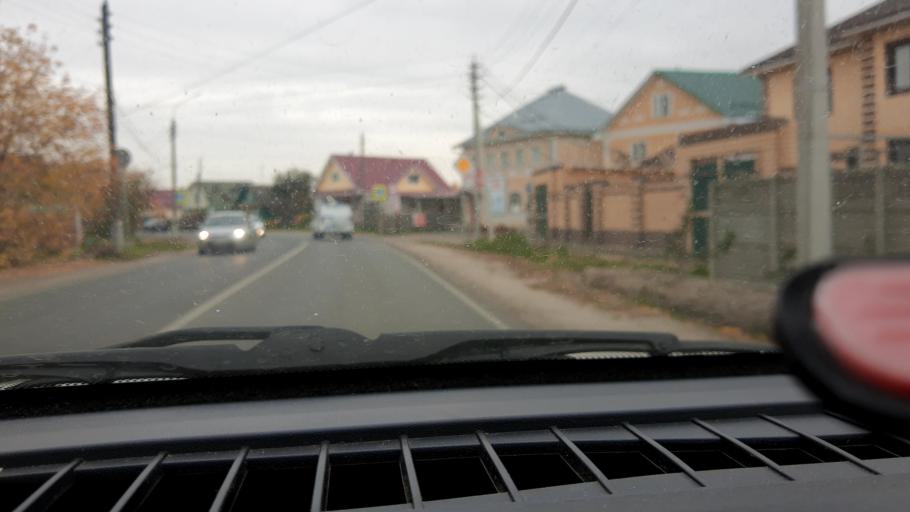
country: RU
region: Nizjnij Novgorod
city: Gorodets
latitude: 56.6457
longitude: 43.4836
